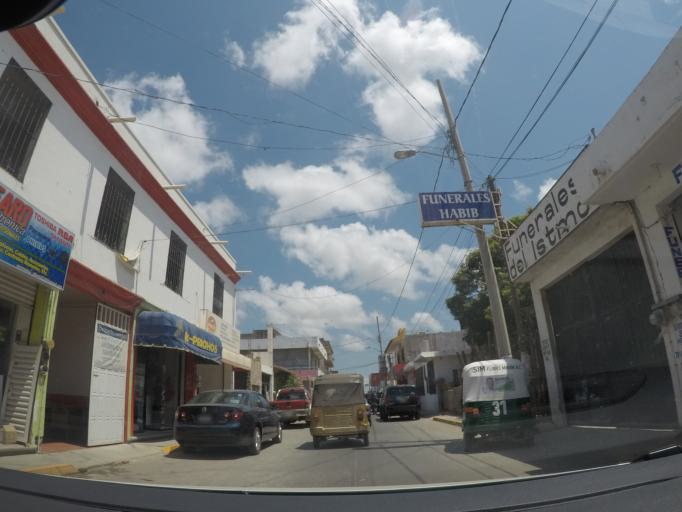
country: MX
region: Oaxaca
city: Juchitan de Zaragoza
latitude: 16.4375
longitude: -95.0223
